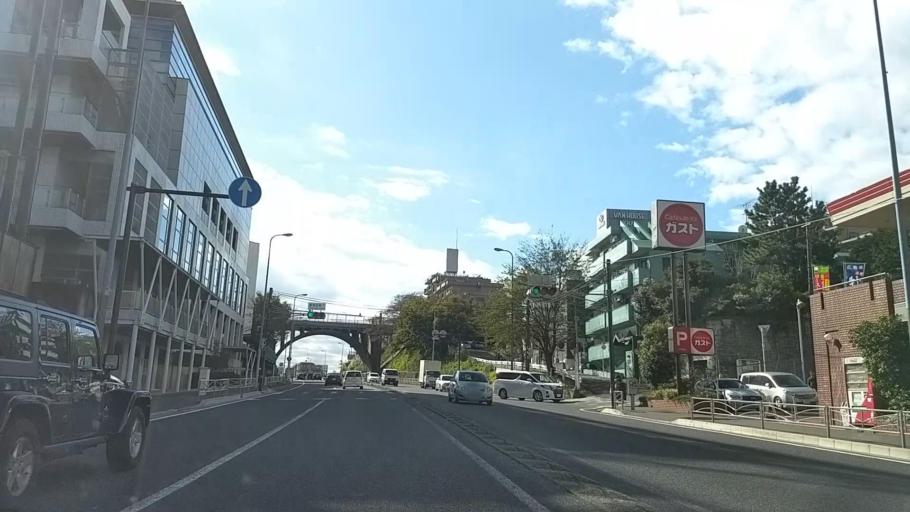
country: JP
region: Kanagawa
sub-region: Kawasaki-shi
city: Kawasaki
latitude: 35.5131
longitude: 139.6637
